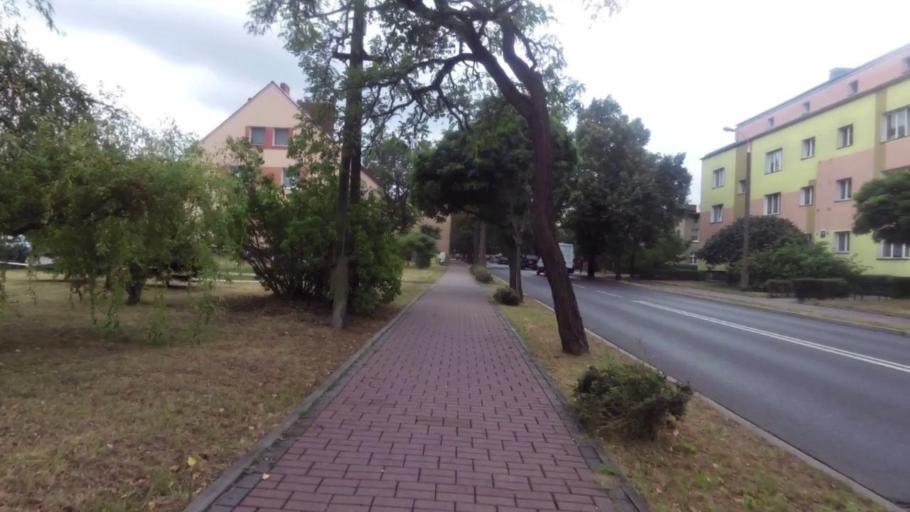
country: PL
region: Lubusz
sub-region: Powiat gorzowski
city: Kostrzyn nad Odra
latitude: 52.5943
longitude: 14.6413
